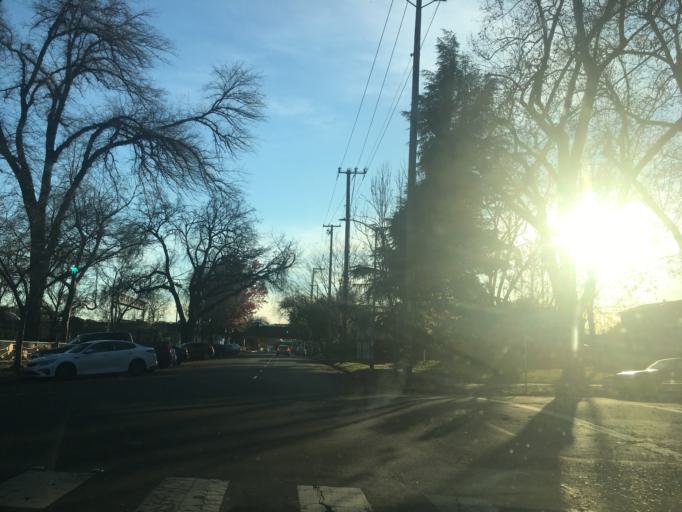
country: US
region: California
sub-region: Sacramento County
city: Sacramento
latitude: 38.5687
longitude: -121.5045
